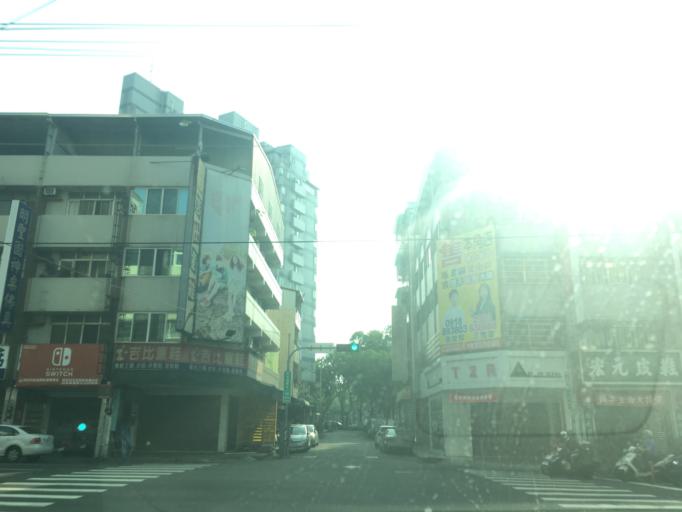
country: TW
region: Taiwan
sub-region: Taichung City
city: Taichung
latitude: 24.1672
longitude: 120.6932
